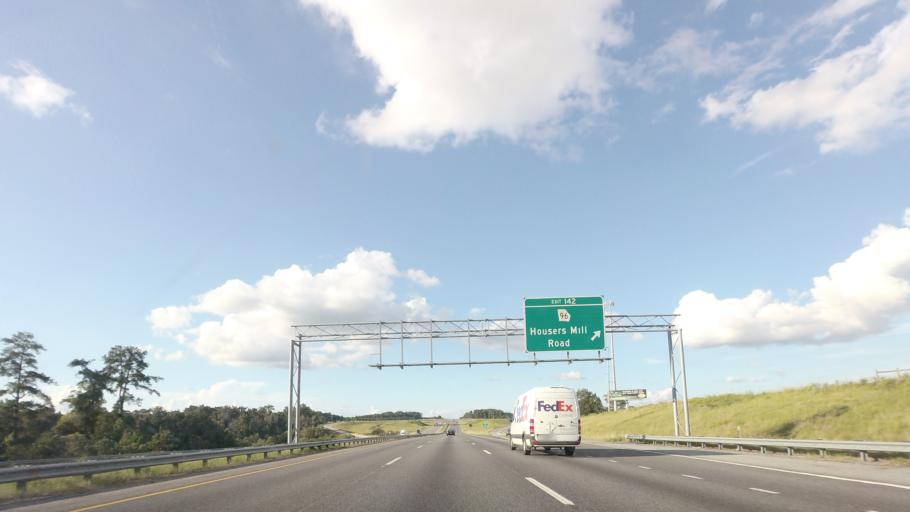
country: US
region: Georgia
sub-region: Houston County
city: Perry
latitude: 32.5405
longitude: -83.7437
